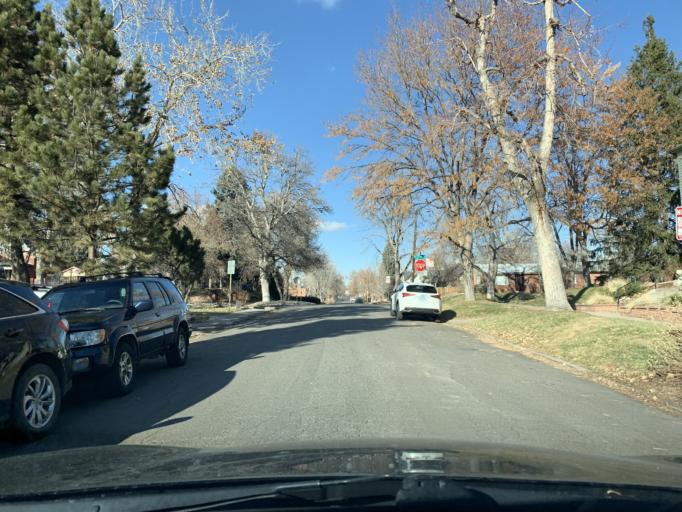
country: US
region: Colorado
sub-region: Jefferson County
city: Edgewater
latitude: 39.7484
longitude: -105.0284
